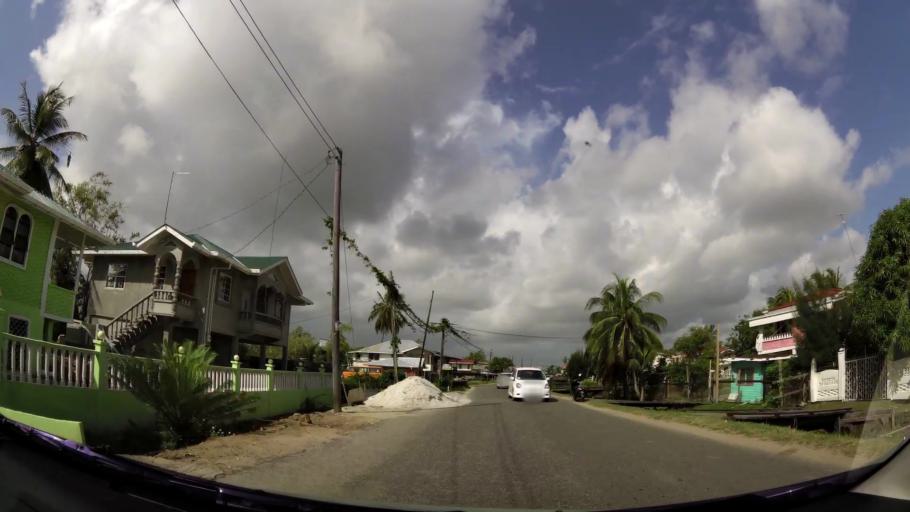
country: GY
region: Demerara-Mahaica
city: Mahaica Village
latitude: 6.6736
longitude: -57.9209
